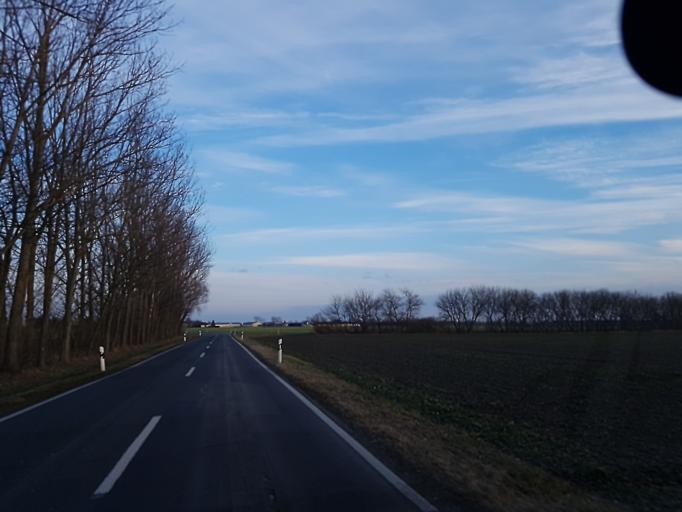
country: DE
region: Brandenburg
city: Juterbog
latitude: 51.9220
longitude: 13.0704
